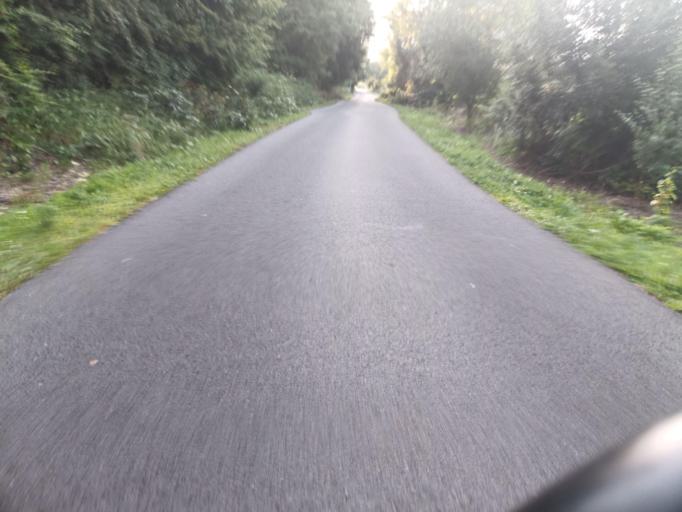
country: GB
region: Northern Ireland
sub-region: Castlereagh District
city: Dundonald
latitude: 54.5900
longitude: -5.8204
